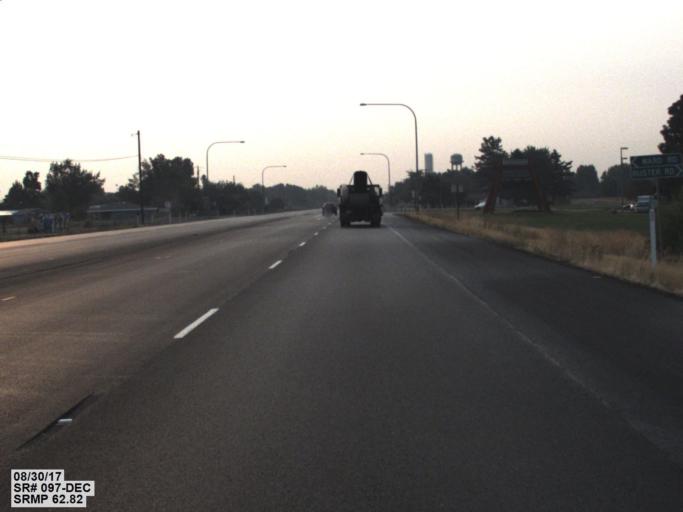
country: US
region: Washington
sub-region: Yakima County
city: Toppenish
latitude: 46.3819
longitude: -120.3432
